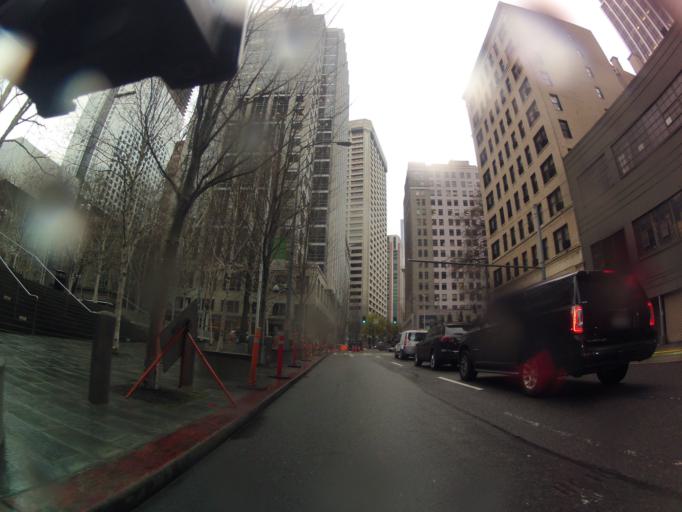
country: US
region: Washington
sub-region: King County
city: Seattle
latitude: 47.6146
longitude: -122.3368
